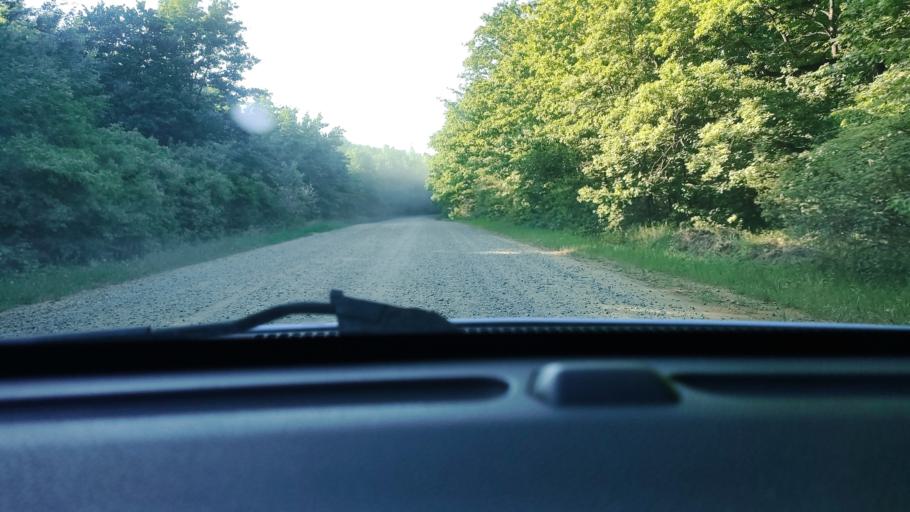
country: RU
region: Krasnodarskiy
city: Goryachiy Klyuch
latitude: 44.7118
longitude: 38.9917
